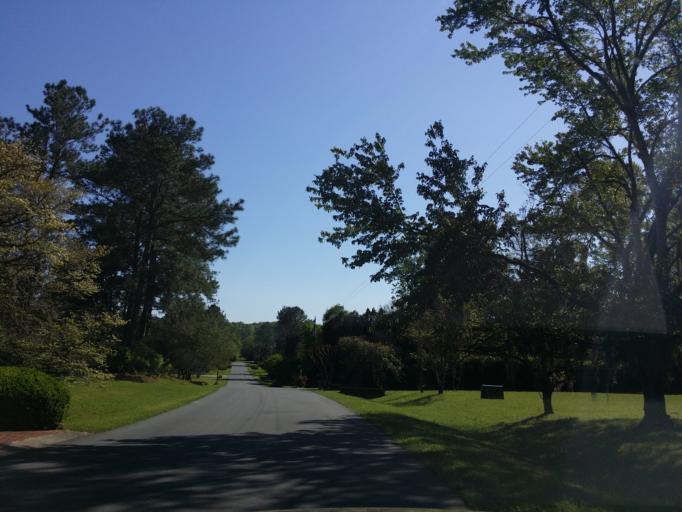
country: US
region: Florida
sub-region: Leon County
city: Tallahassee
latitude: 30.4856
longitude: -84.1901
